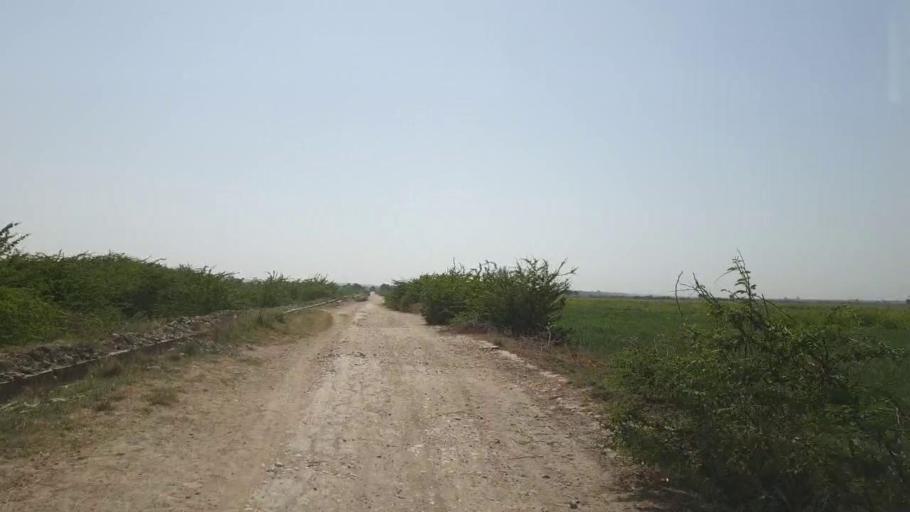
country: PK
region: Sindh
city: Naukot
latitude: 24.9042
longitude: 69.4875
